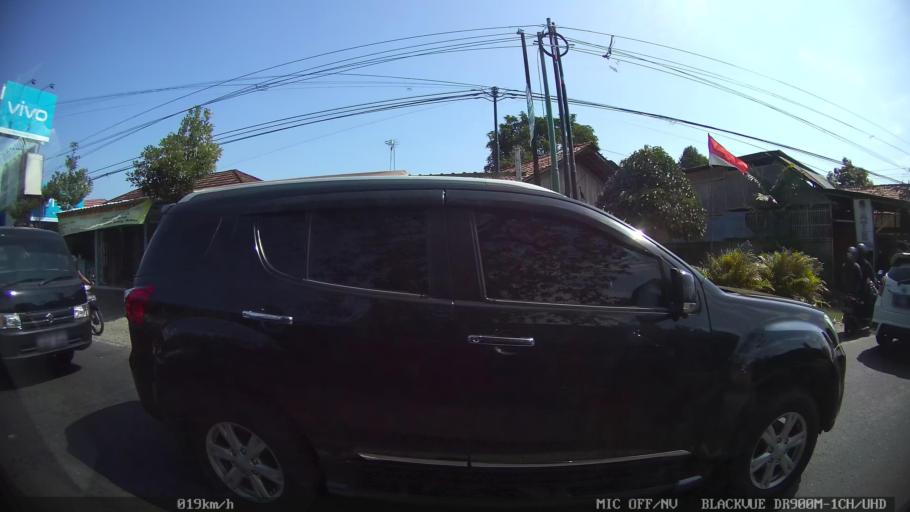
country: ID
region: Daerah Istimewa Yogyakarta
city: Sewon
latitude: -7.9139
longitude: 110.3730
